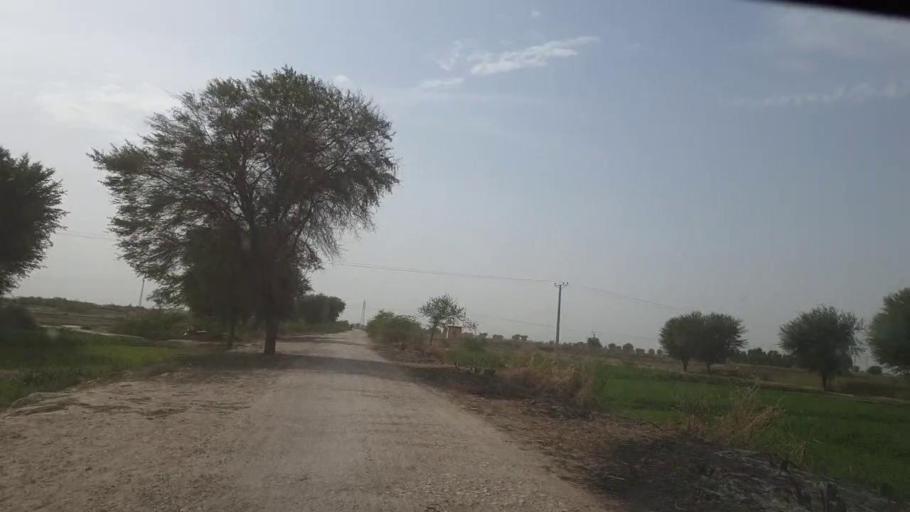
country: PK
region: Sindh
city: Nabisar
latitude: 25.0381
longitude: 69.5161
